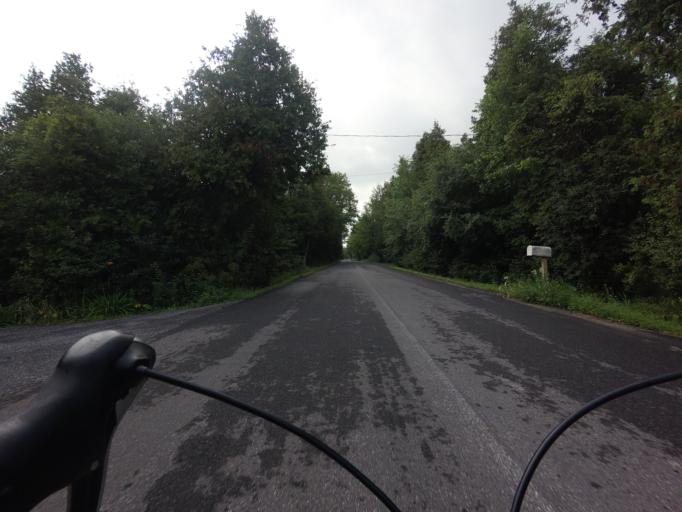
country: CA
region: Ontario
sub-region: Lanark County
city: Smiths Falls
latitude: 44.9579
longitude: -75.8014
